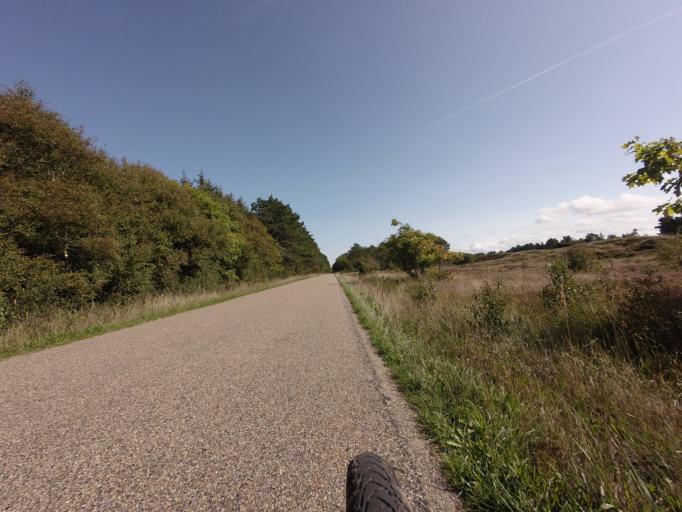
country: DK
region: North Denmark
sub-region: Hjorring Kommune
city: Hirtshals
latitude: 57.5793
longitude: 10.0161
